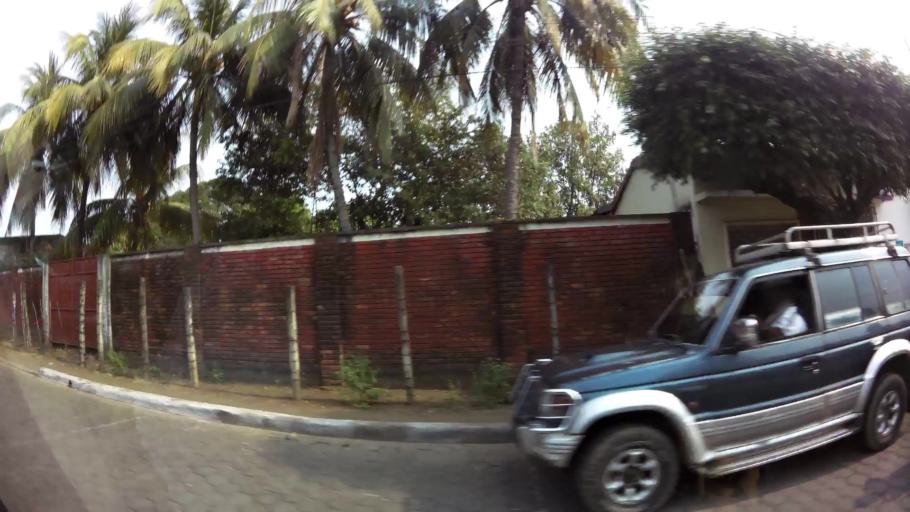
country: NI
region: Chinandega
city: Chinandega
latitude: 12.6283
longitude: -87.1239
